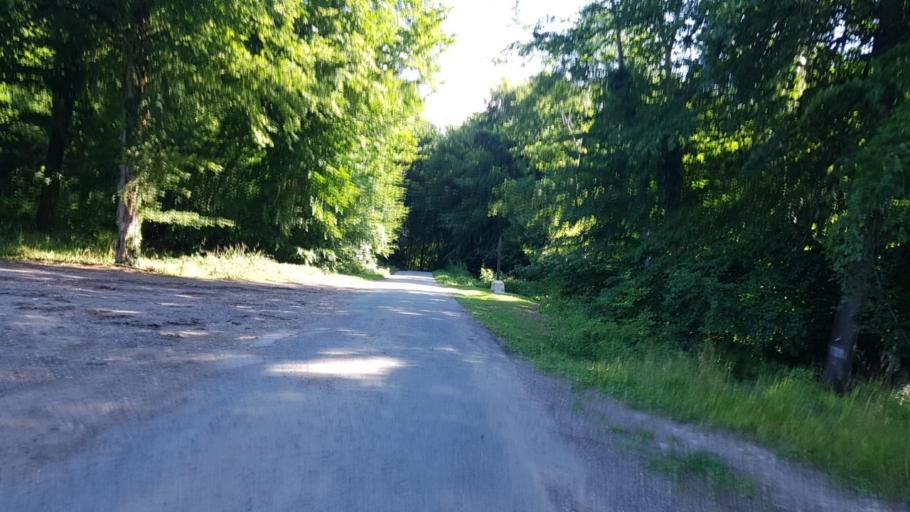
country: FR
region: Picardie
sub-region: Departement de l'Oise
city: Fleurines
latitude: 49.2562
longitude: 2.6194
